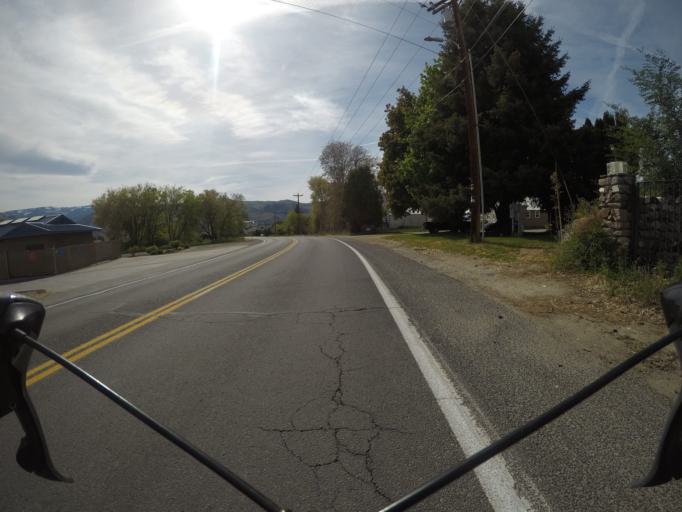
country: US
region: Washington
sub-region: Douglas County
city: East Wenatchee Bench
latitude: 47.4132
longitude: -120.2769
